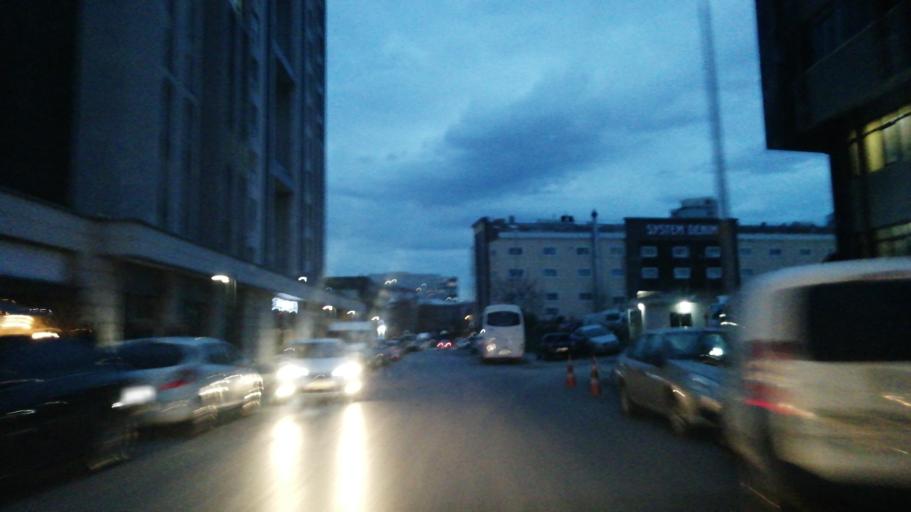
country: TR
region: Istanbul
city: Mahmutbey
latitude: 41.0204
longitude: 28.8240
